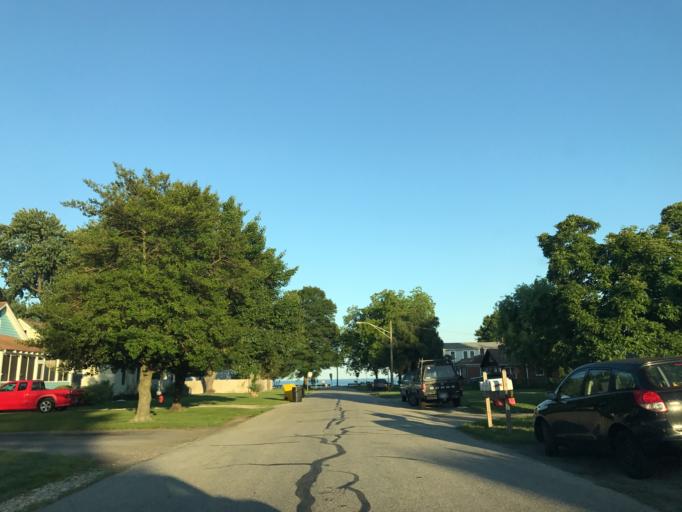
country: US
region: Maryland
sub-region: Anne Arundel County
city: Mayo
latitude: 38.8756
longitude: -76.5065
